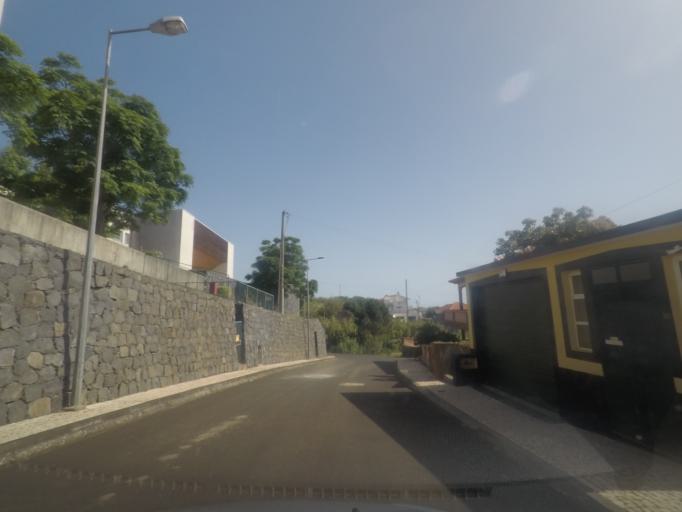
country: PT
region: Madeira
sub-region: Calheta
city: Faja da Ovelha
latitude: 32.8112
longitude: -17.2488
